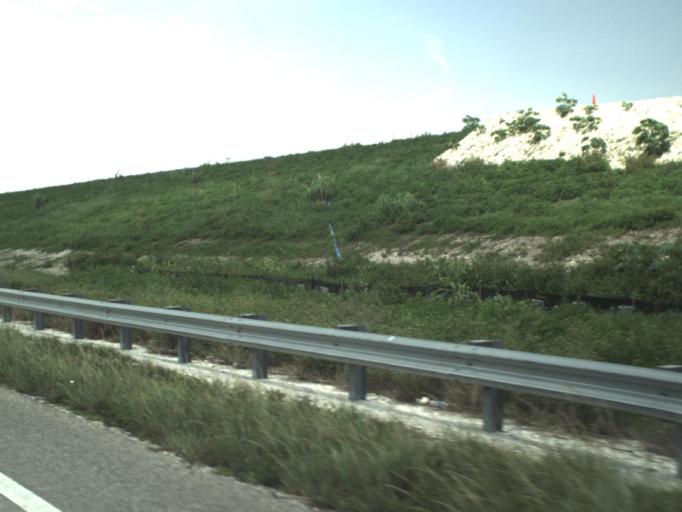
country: US
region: Florida
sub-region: Palm Beach County
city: South Bay
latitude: 26.7029
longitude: -80.8270
